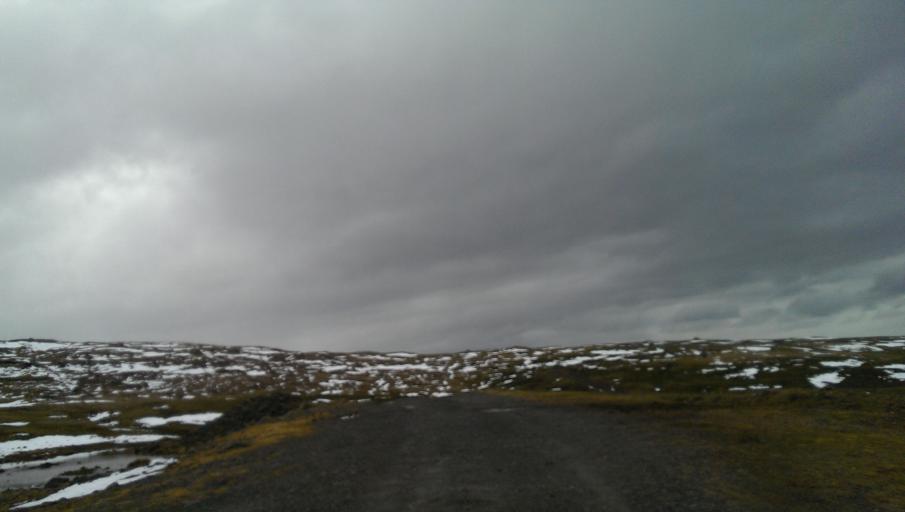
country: FO
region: Streymoy
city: Hoyvik
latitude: 62.0344
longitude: -6.8054
